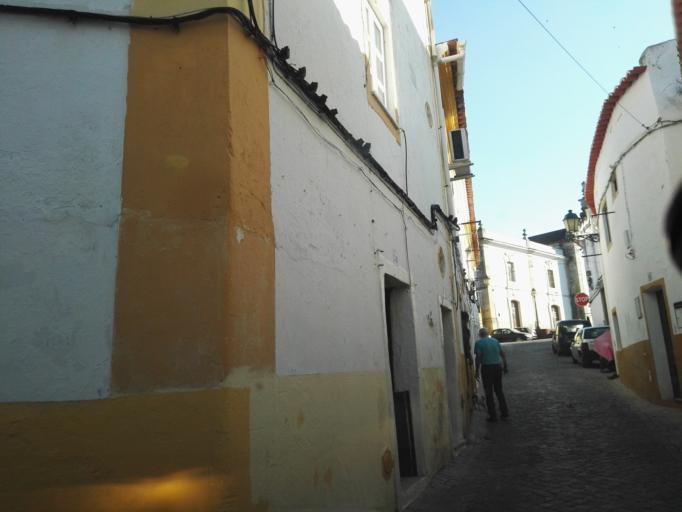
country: PT
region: Portalegre
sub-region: Elvas
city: Elvas
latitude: 38.8802
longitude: -7.1602
